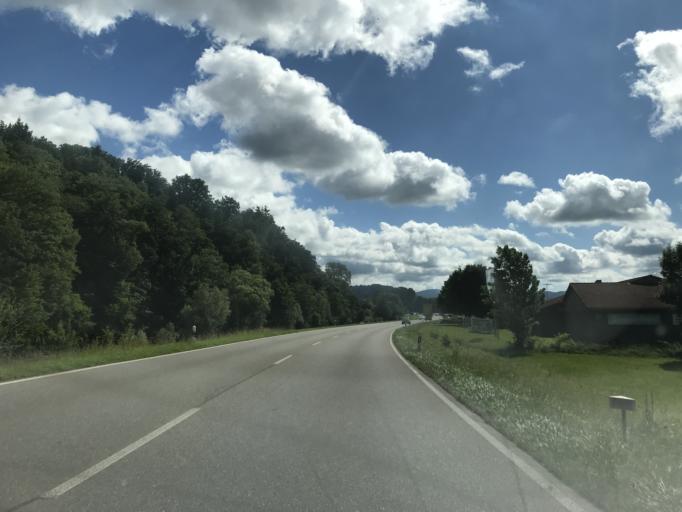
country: DE
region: Baden-Wuerttemberg
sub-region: Freiburg Region
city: Maulburg
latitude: 47.6456
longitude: 7.7646
